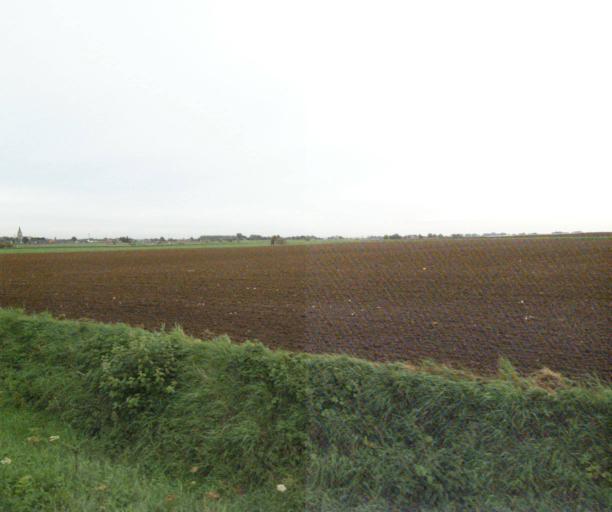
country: FR
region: Nord-Pas-de-Calais
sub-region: Departement du Nord
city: Aubers
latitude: 50.5858
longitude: 2.8167
